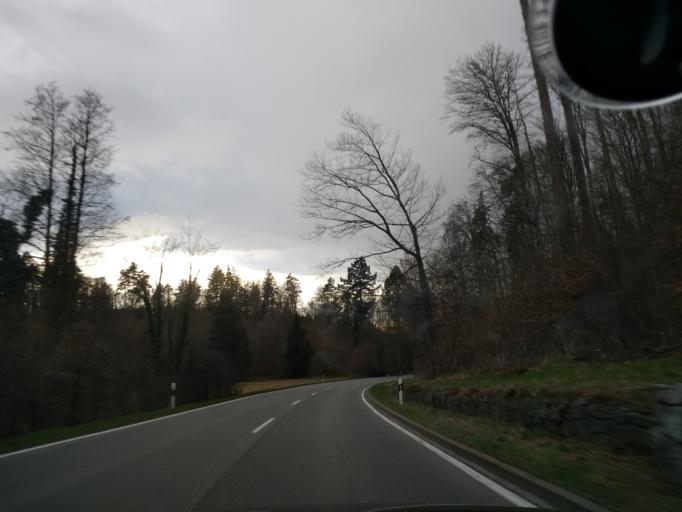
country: DE
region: Baden-Wuerttemberg
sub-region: Freiburg Region
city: Allensbach
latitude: 47.7263
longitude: 9.1241
